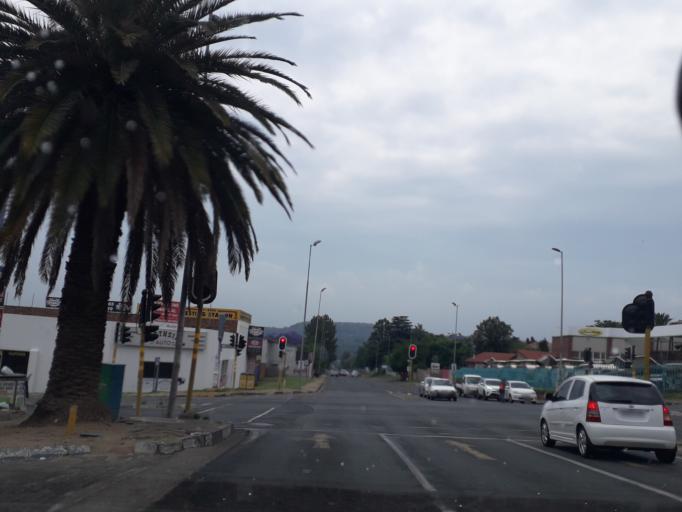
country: ZA
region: Gauteng
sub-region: City of Johannesburg Metropolitan Municipality
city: Johannesburg
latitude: -26.1045
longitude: 27.9767
